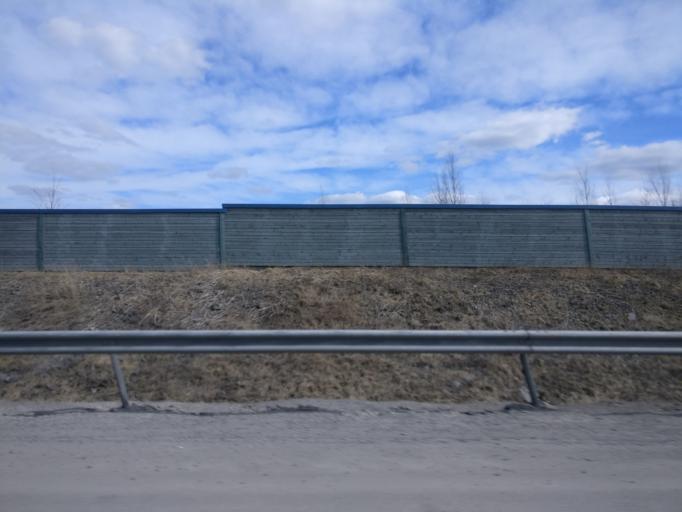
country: FI
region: Pirkanmaa
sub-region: Tampere
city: Lempaeaelae
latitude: 61.3749
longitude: 23.7906
